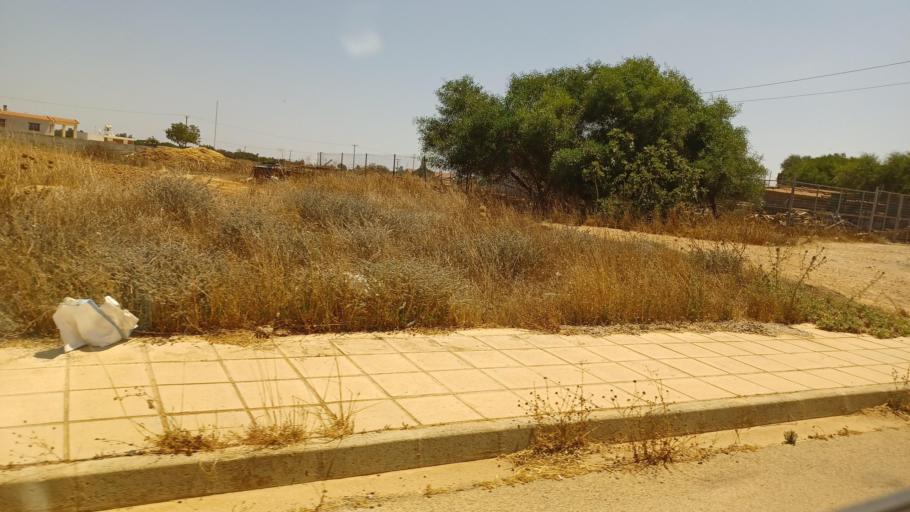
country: CY
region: Ammochostos
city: Acheritou
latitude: 35.0711
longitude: 33.8871
